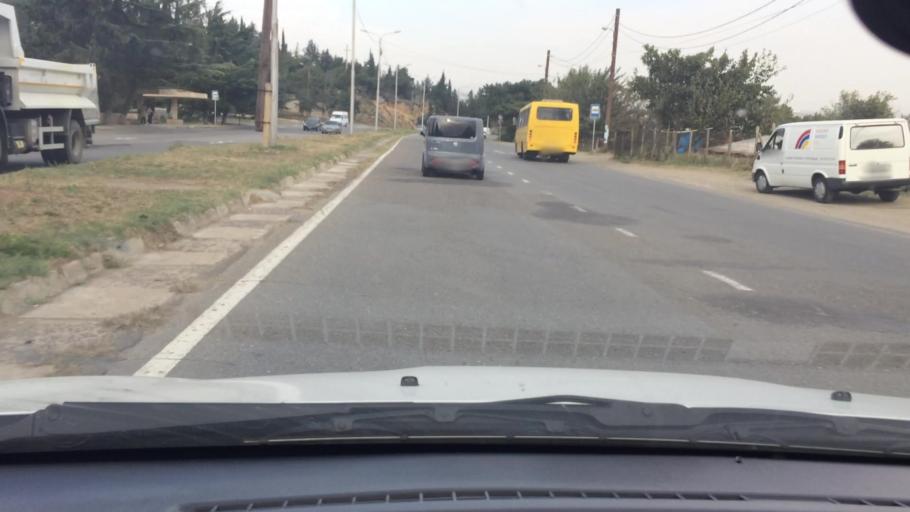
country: GE
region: T'bilisi
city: Tbilisi
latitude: 41.6484
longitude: 44.9013
